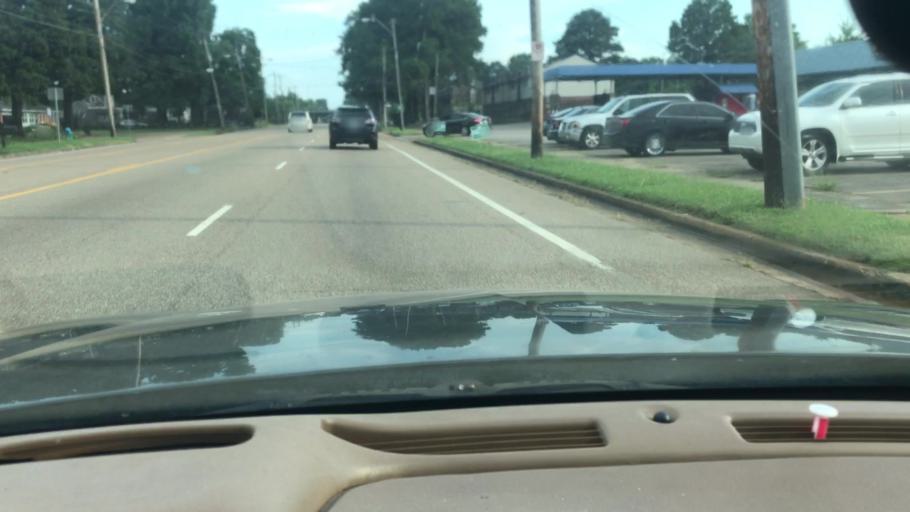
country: US
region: Mississippi
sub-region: De Soto County
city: Southaven
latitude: 35.0490
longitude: -90.0075
